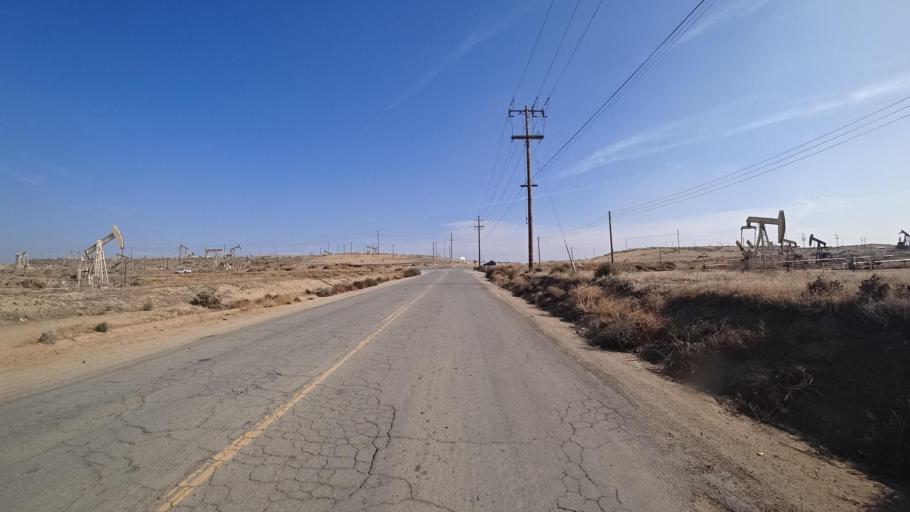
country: US
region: California
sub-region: Kern County
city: Oildale
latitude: 35.5299
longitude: -119.0838
